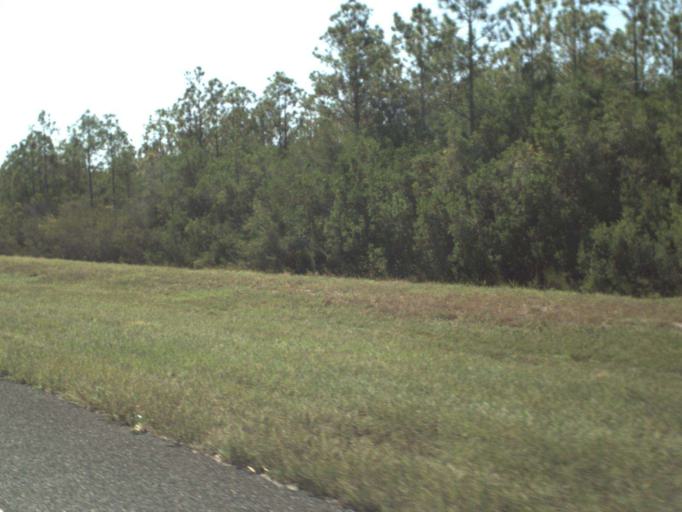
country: US
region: Florida
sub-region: Walton County
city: Seaside
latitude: 30.3010
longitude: -86.0292
